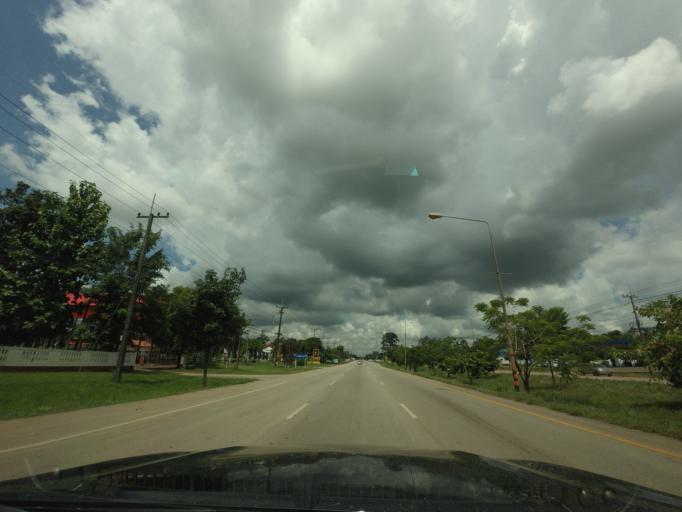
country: TH
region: Changwat Udon Thani
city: Udon Thani
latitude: 17.5430
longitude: 102.8003
